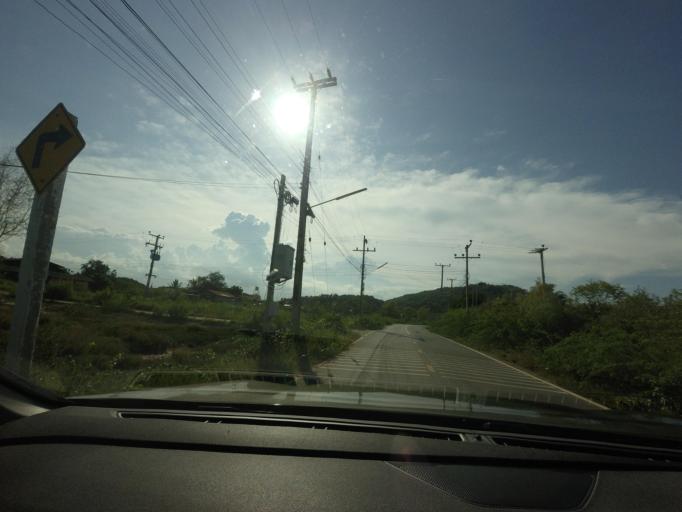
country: TH
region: Prachuap Khiri Khan
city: Pran Buri
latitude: 12.4064
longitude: 99.9836
